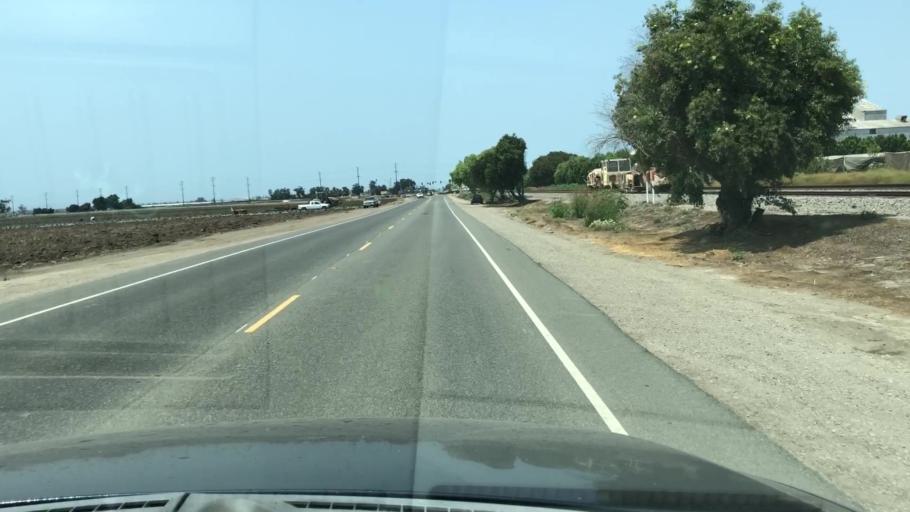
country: US
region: California
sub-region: Ventura County
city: Camarillo
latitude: 34.1966
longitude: -119.0995
